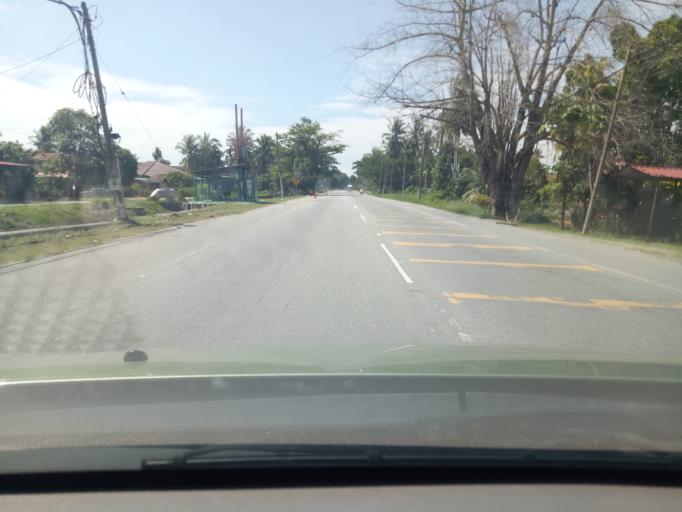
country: MY
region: Kedah
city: Gurun
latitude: 5.9295
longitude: 100.4179
